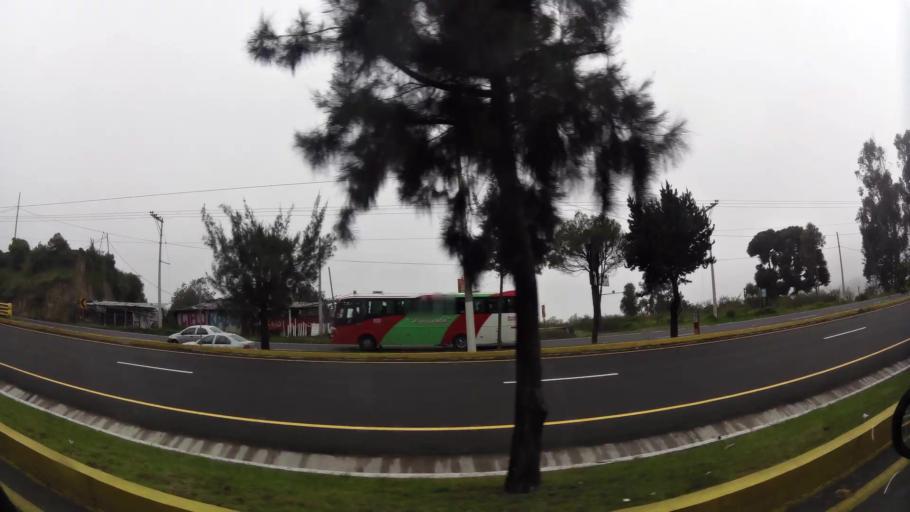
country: EC
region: Pichincha
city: Quito
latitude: -0.2690
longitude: -78.4871
